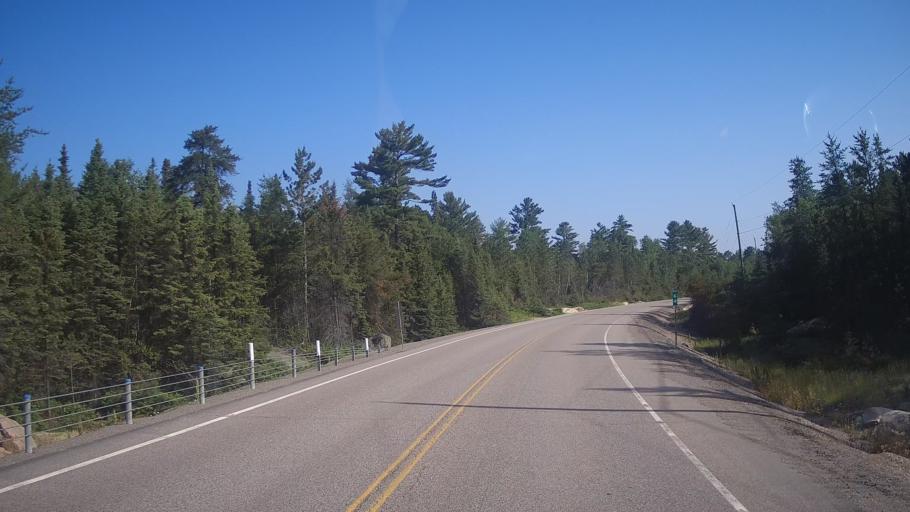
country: CA
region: Ontario
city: Rayside-Balfour
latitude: 46.7459
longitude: -81.6012
